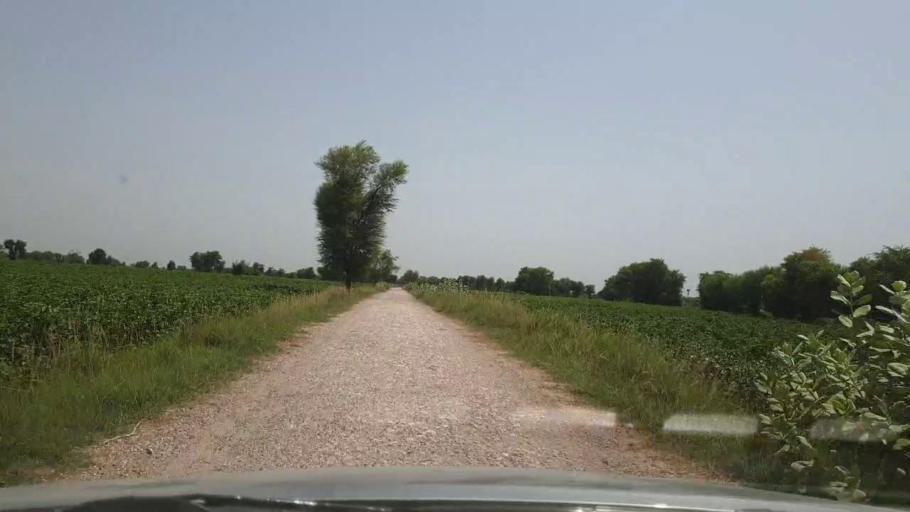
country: PK
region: Sindh
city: Pano Aqil
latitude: 27.7975
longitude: 69.2429
